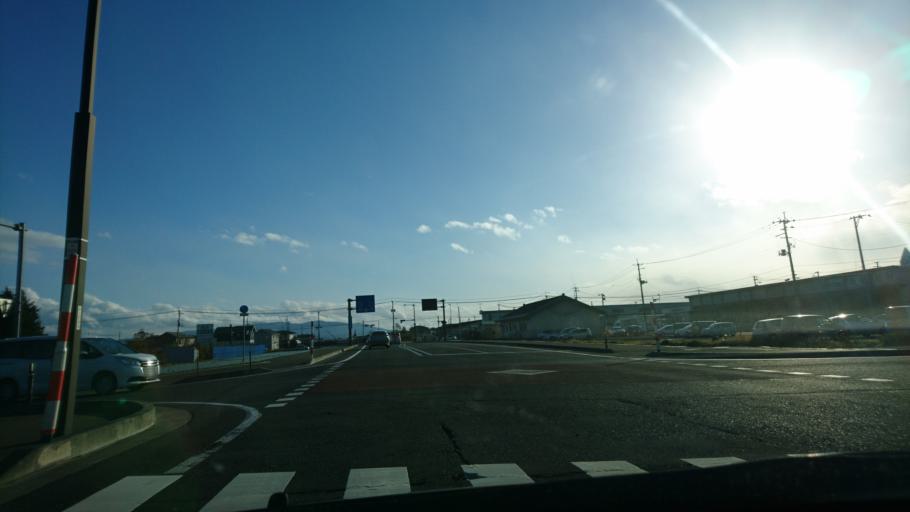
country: JP
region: Iwate
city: Mizusawa
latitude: 39.1371
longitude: 141.1626
